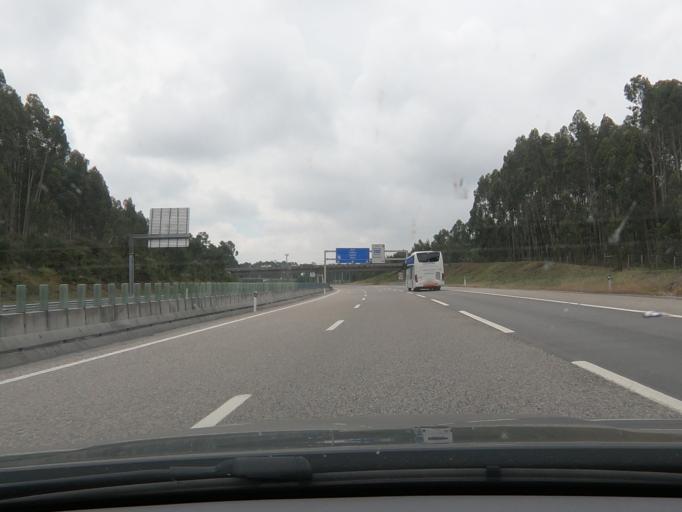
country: PT
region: Leiria
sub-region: Pombal
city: Lourical
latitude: 39.9950
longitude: -8.7982
